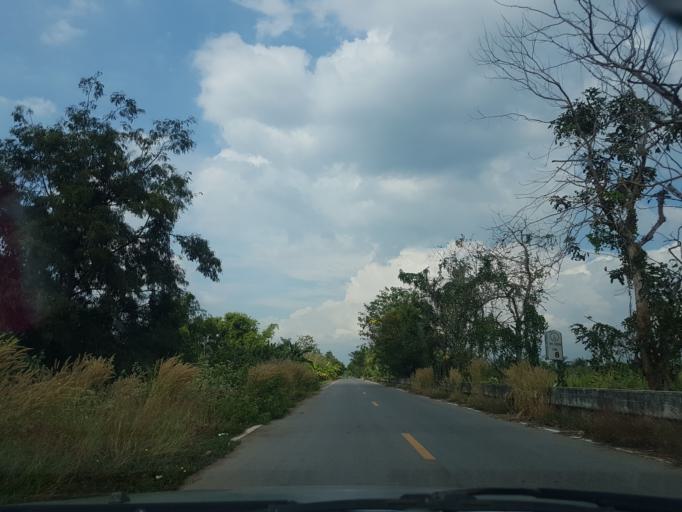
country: TH
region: Sara Buri
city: Nong Khae
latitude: 14.2393
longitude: 100.8913
